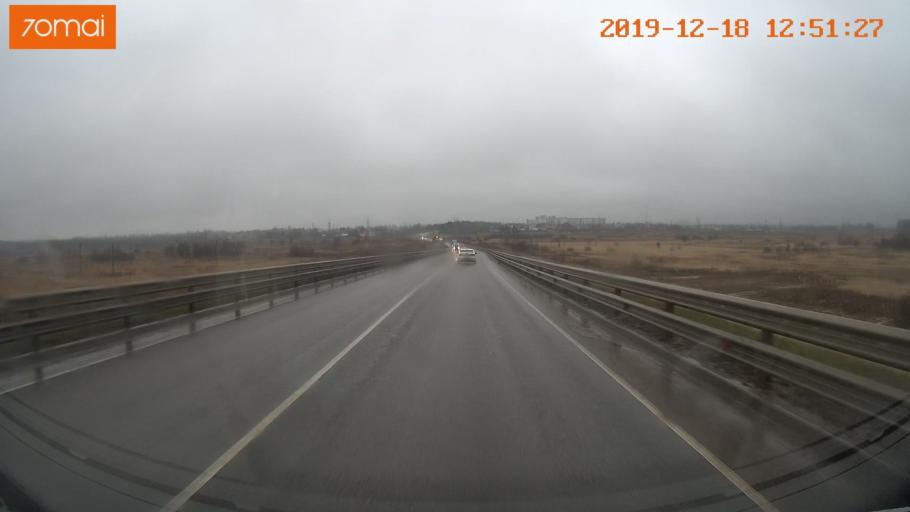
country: RU
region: Moskovskaya
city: Klin
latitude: 56.3034
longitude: 36.6838
